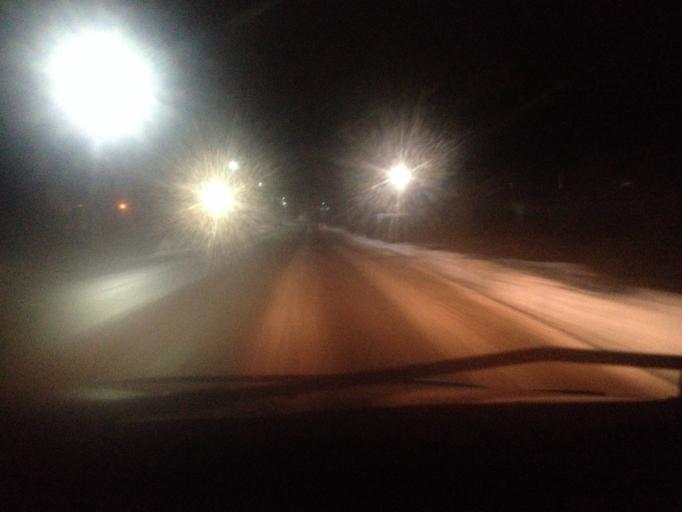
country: RU
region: Tula
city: Leninskiy
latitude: 54.2821
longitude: 37.4599
